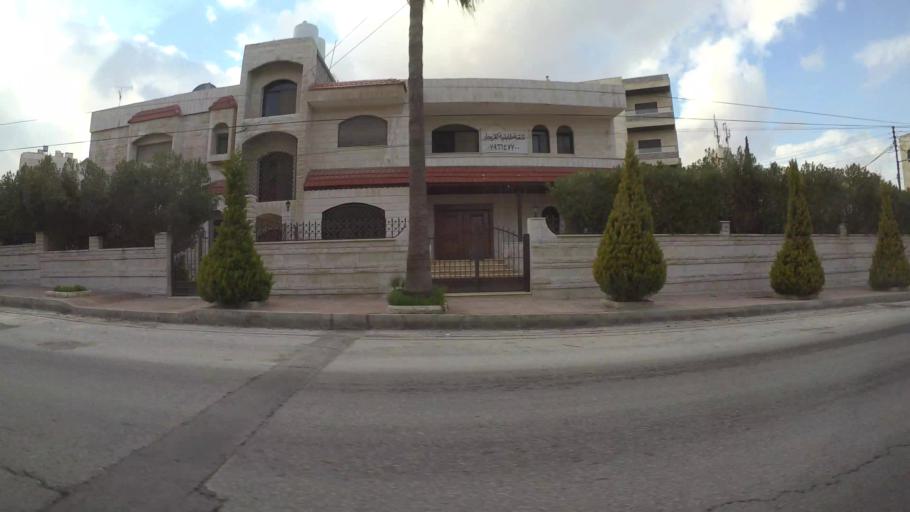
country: JO
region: Amman
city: Al Jubayhah
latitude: 31.9795
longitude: 35.8614
